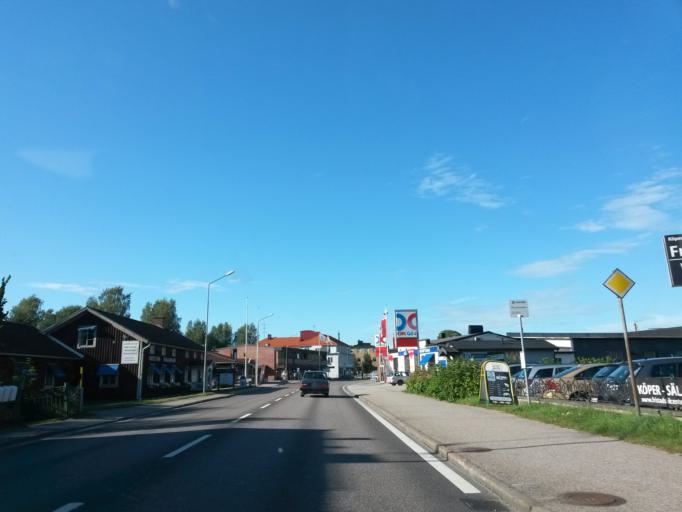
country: SE
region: Vaestra Goetaland
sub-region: Boras Kommun
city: Boras
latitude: 57.8235
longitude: 13.0080
